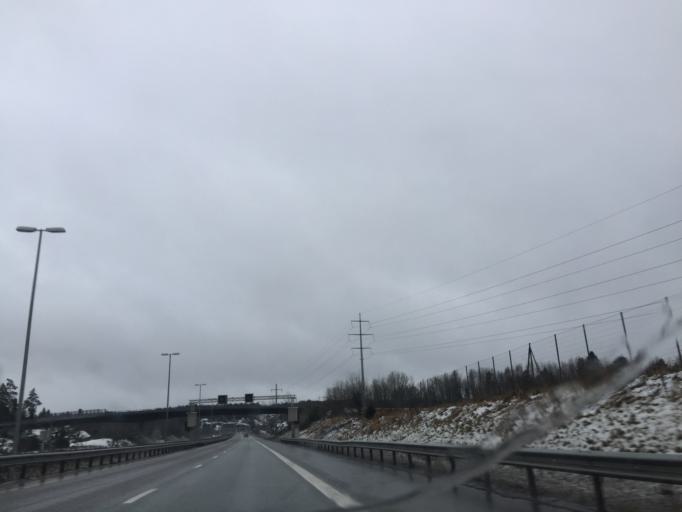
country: NO
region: Akershus
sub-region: Vestby
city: Vestby
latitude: 59.5442
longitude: 10.7244
